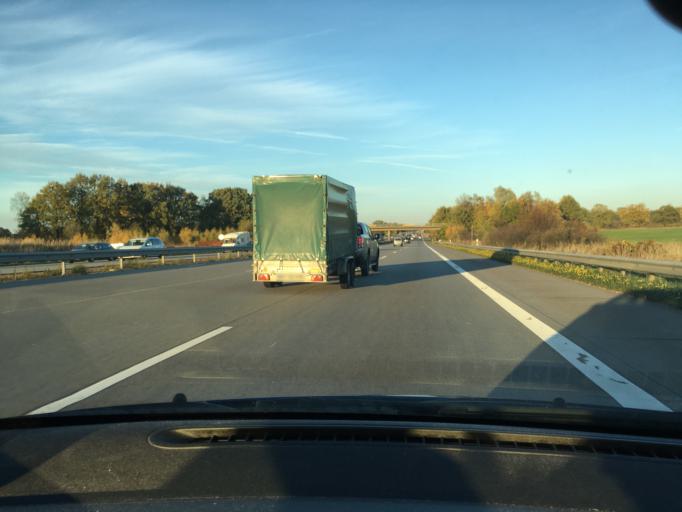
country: DE
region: Schleswig-Holstein
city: Stapelfeld
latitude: 53.5860
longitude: 10.2112
